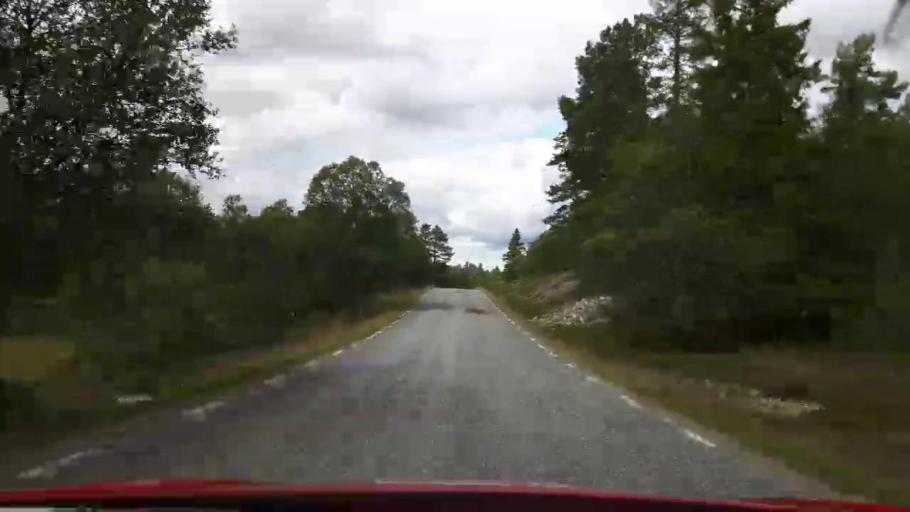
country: NO
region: Hedmark
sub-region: Trysil
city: Innbygda
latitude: 62.1124
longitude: 12.9769
